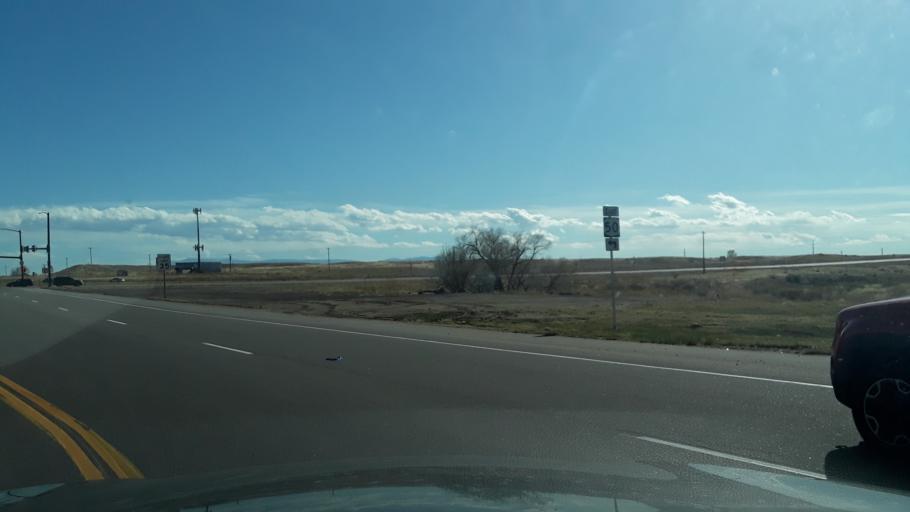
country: US
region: Colorado
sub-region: Pueblo County
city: Pueblo West
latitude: 38.3155
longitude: -104.6606
